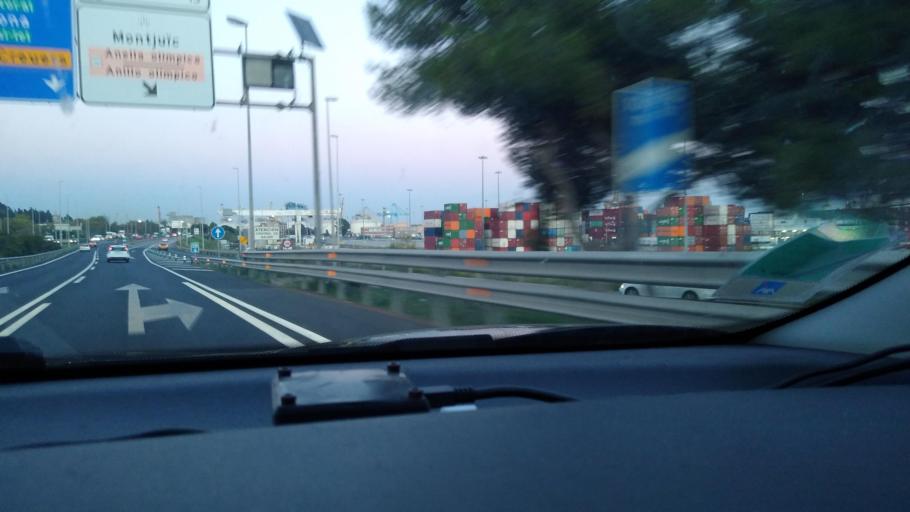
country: ES
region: Catalonia
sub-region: Provincia de Barcelona
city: Sants-Montjuic
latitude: 41.3502
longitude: 2.1478
